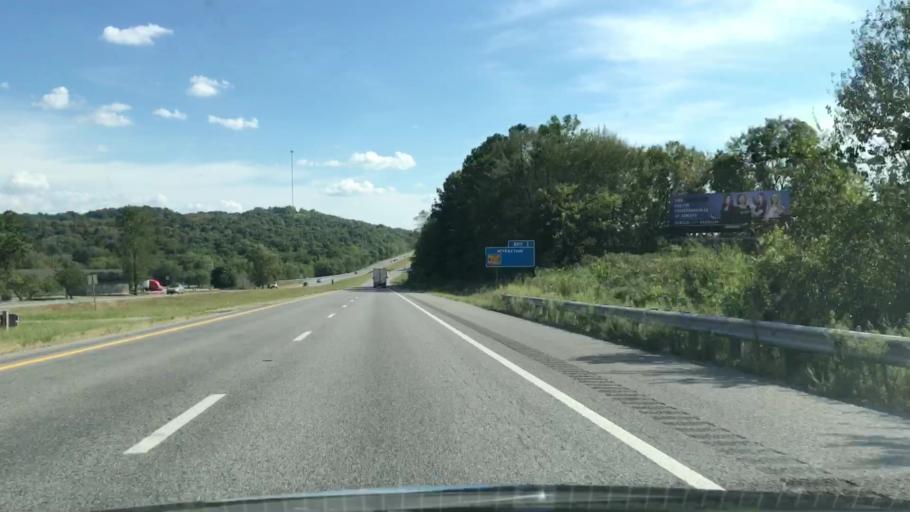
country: US
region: Alabama
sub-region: Limestone County
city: Ardmore
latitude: 35.0380
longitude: -86.8794
